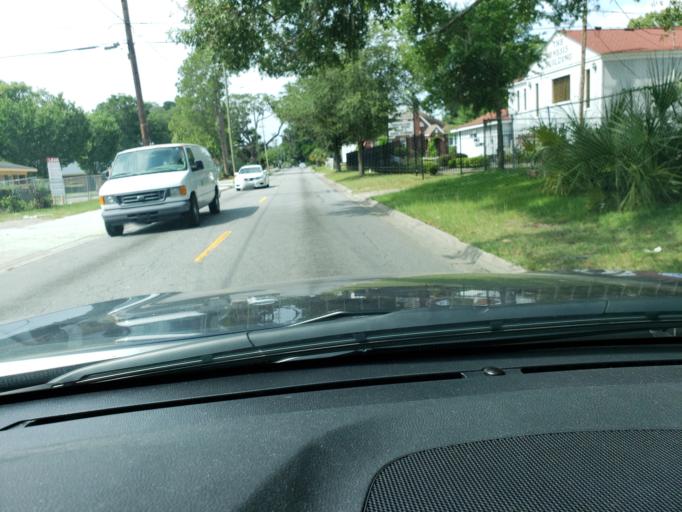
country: US
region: Georgia
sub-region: Chatham County
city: Thunderbolt
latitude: 32.0405
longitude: -81.0883
